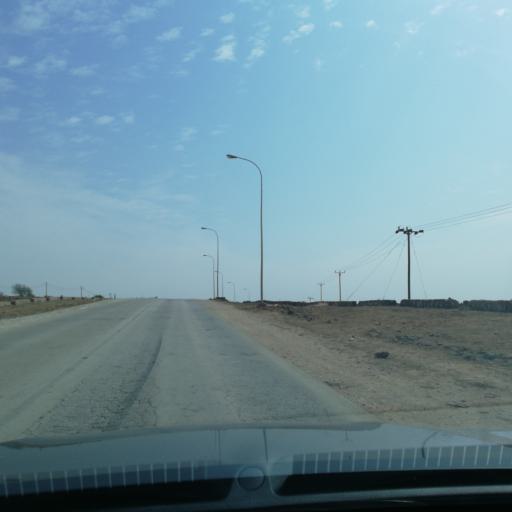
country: OM
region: Zufar
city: Salalah
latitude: 17.2375
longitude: 54.0534
